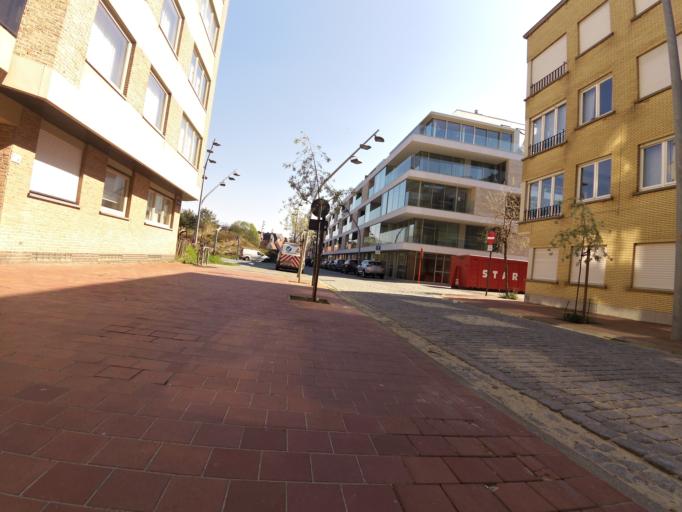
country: BE
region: Flanders
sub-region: Provincie West-Vlaanderen
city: Knokke-Heist
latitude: 51.3518
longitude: 3.2932
